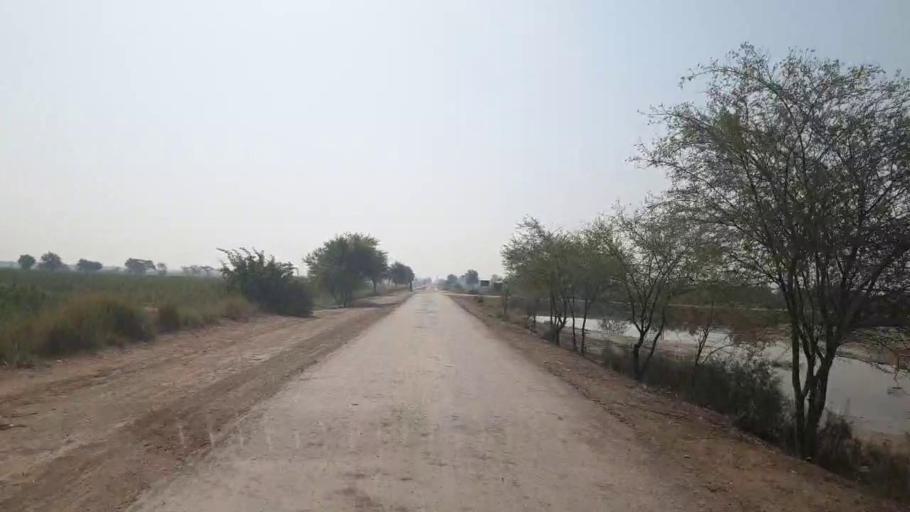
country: PK
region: Sindh
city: Shahdadpur
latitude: 25.9216
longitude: 68.7360
